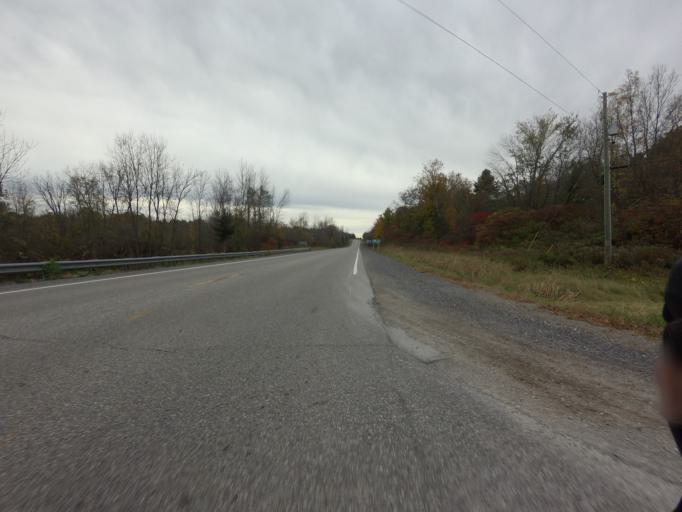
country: CA
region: Ontario
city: Gananoque
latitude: 44.4036
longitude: -76.3121
